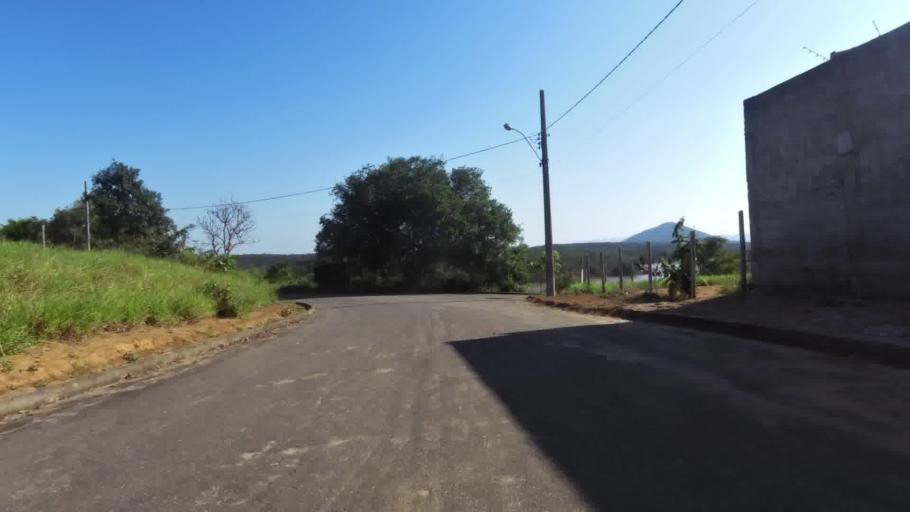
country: BR
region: Espirito Santo
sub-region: Guarapari
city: Guarapari
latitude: -20.7424
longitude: -40.5587
